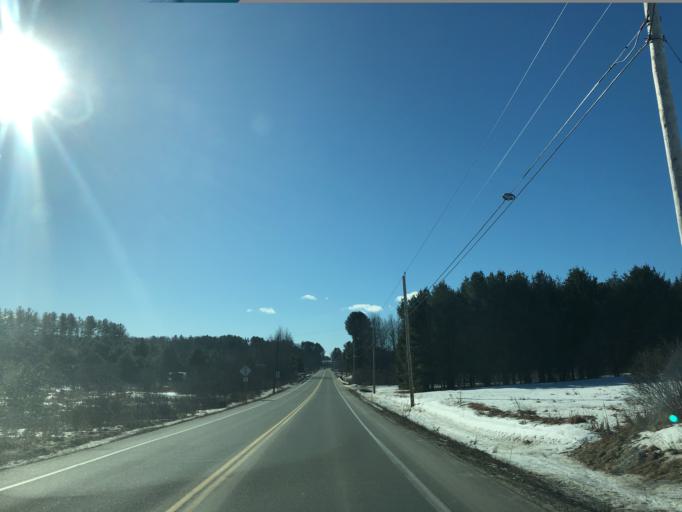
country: US
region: Maine
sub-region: Cumberland County
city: North Windham
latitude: 43.7981
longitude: -70.4402
